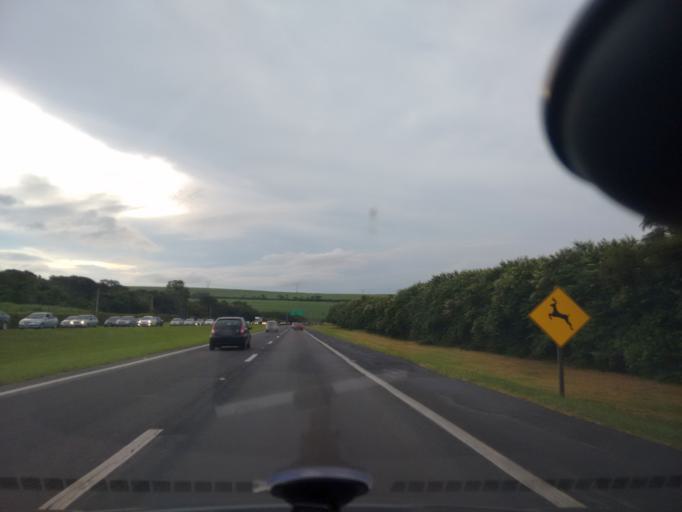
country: BR
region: Sao Paulo
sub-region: Itirapina
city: Itirapina
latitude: -22.2224
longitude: -47.7591
